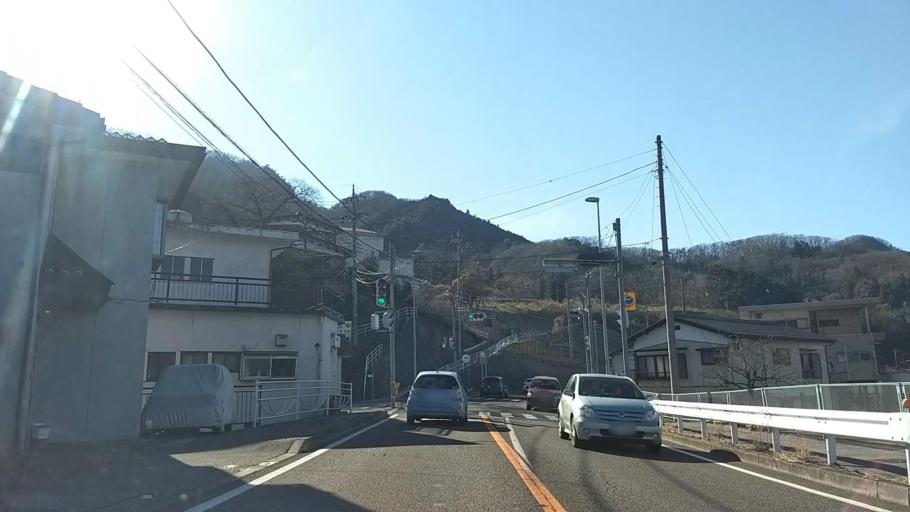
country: JP
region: Yamanashi
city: Otsuki
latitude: 35.6117
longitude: 138.9657
